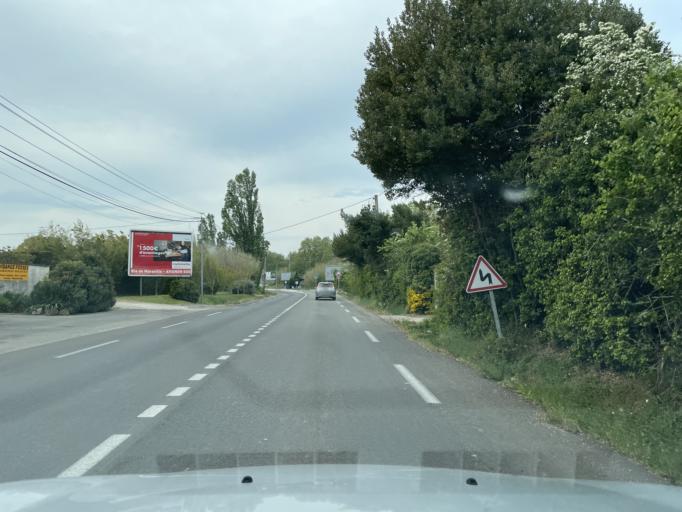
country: FR
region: Provence-Alpes-Cote d'Azur
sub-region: Departement des Bouches-du-Rhone
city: Tarascon
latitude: 43.8143
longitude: 4.6727
